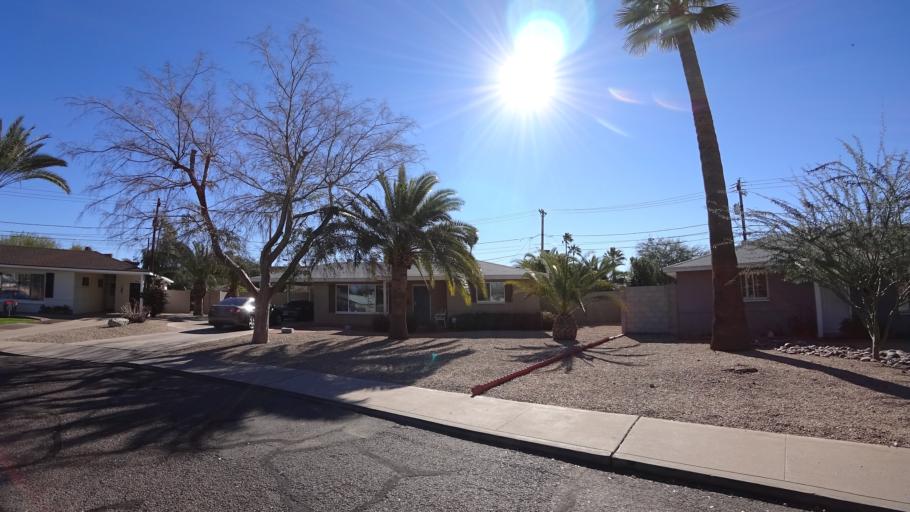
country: US
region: Arizona
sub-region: Maricopa County
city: Phoenix
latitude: 33.5027
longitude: -112.0403
